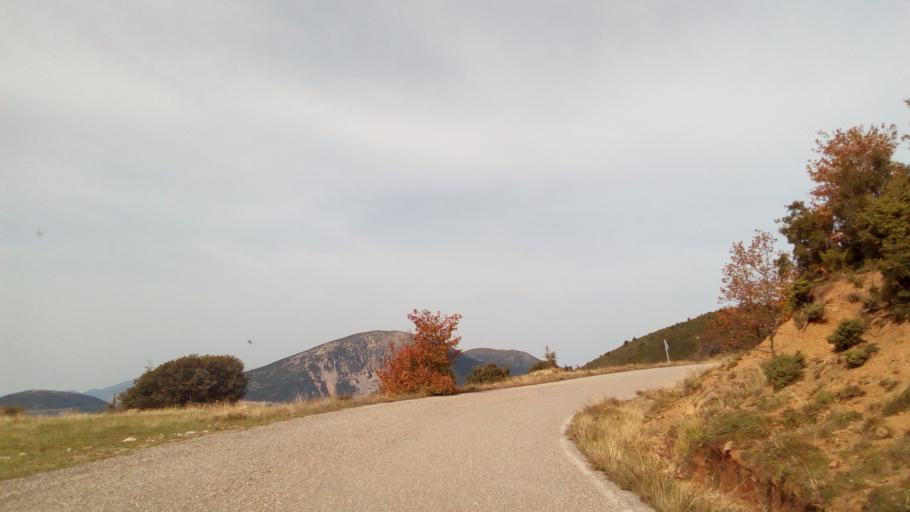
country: GR
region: West Greece
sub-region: Nomos Aitolias kai Akarnanias
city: Thermo
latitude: 38.5615
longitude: 21.8225
